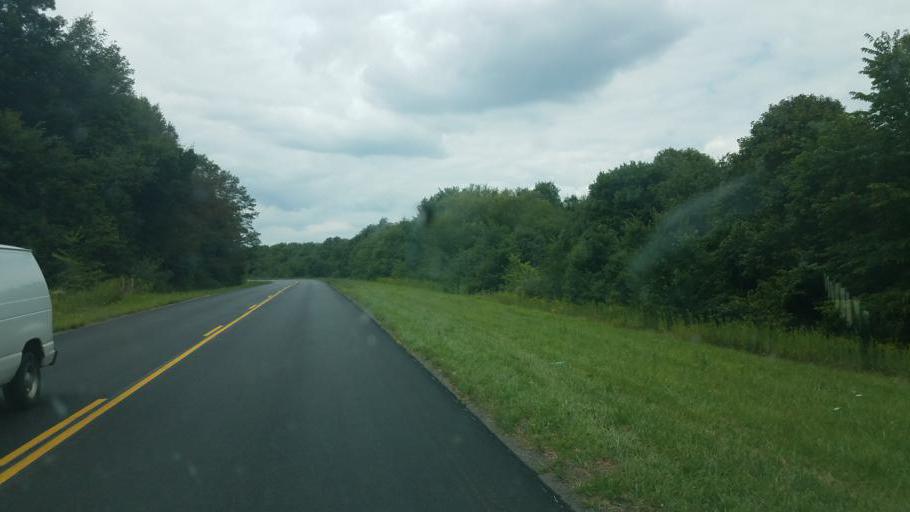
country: US
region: Ohio
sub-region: Columbiana County
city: New Waterford
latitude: 40.7957
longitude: -80.6476
